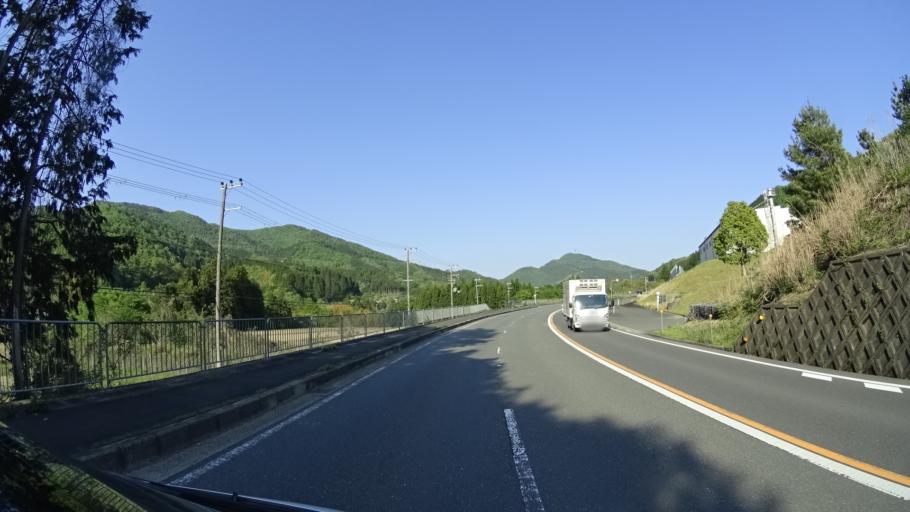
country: JP
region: Kyoto
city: Ayabe
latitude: 35.2087
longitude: 135.2695
